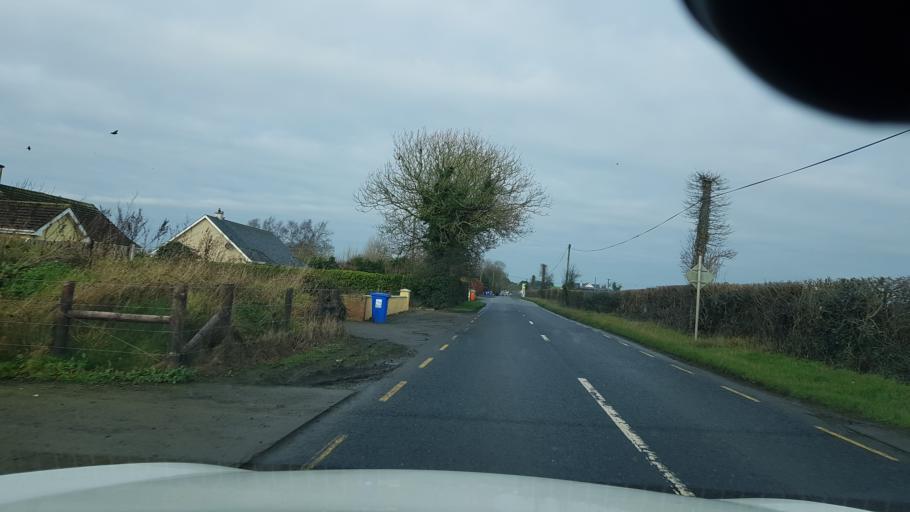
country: IE
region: Leinster
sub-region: An Mhi
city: Navan
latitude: 53.6983
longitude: -6.6787
